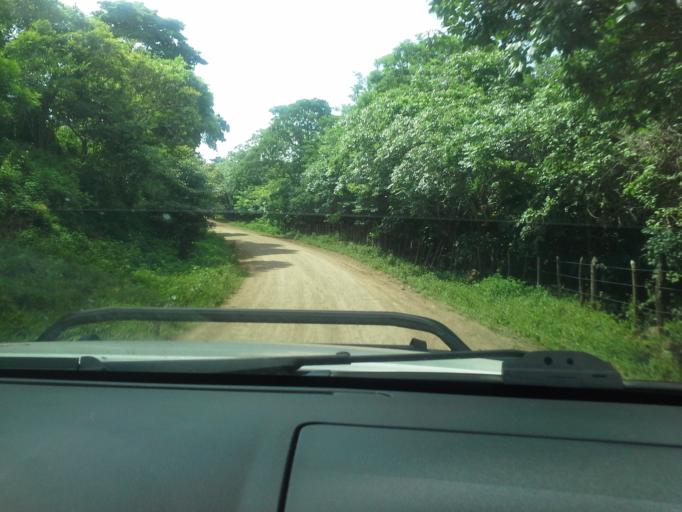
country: NI
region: Matagalpa
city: Terrabona
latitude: 12.7120
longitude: -85.9608
